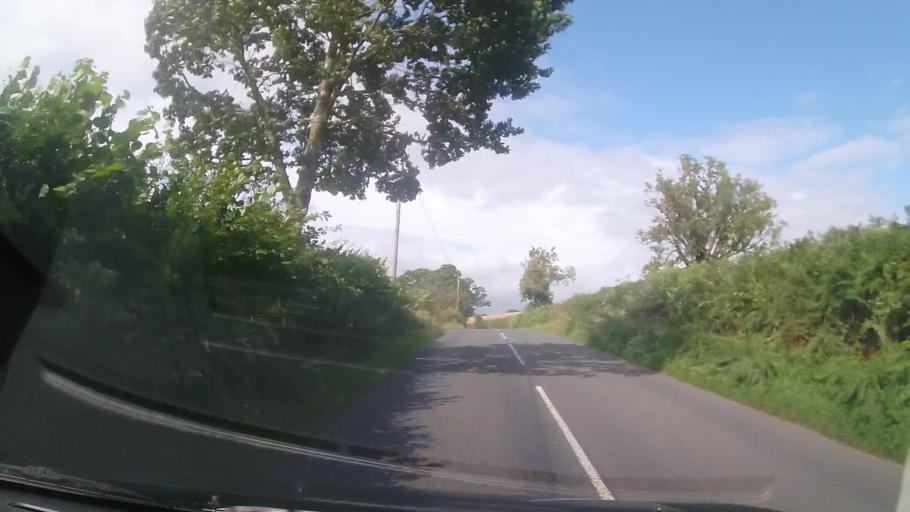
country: GB
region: England
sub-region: Shropshire
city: Acton
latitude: 52.4402
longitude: -3.0356
